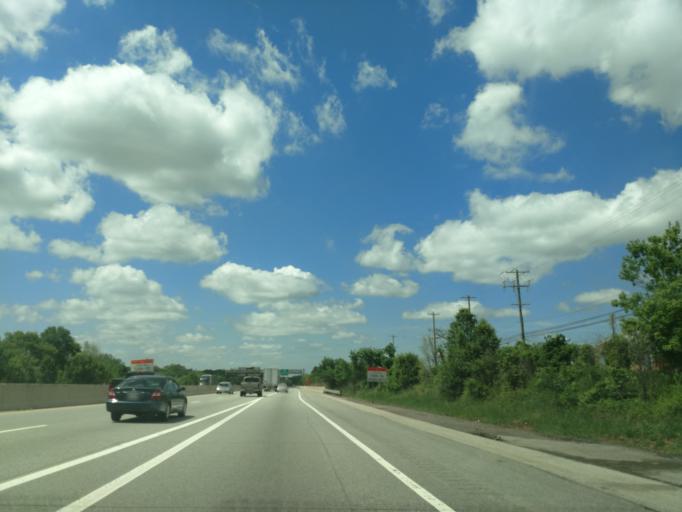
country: US
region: Pennsylvania
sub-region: Montgomery County
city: King of Prussia
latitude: 40.0830
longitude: -75.4094
